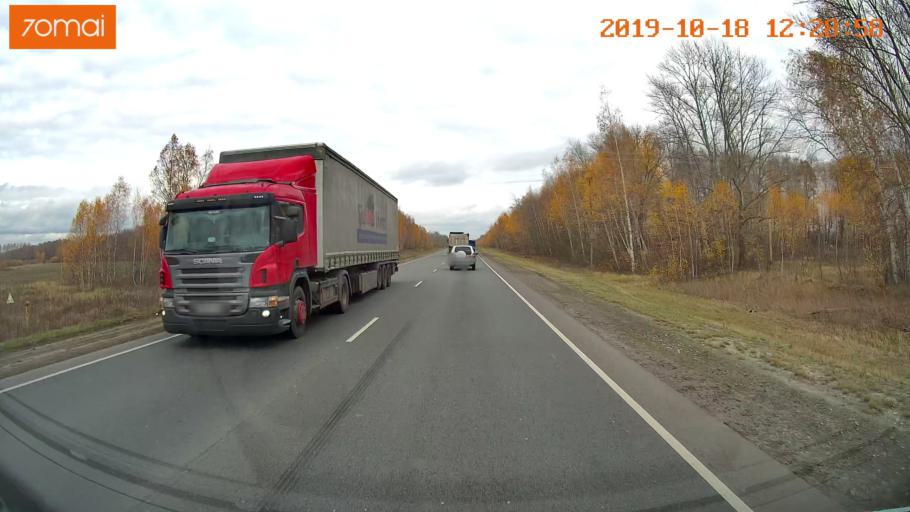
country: RU
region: Rjazan
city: Ryazan'
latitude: 54.5755
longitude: 39.5769
